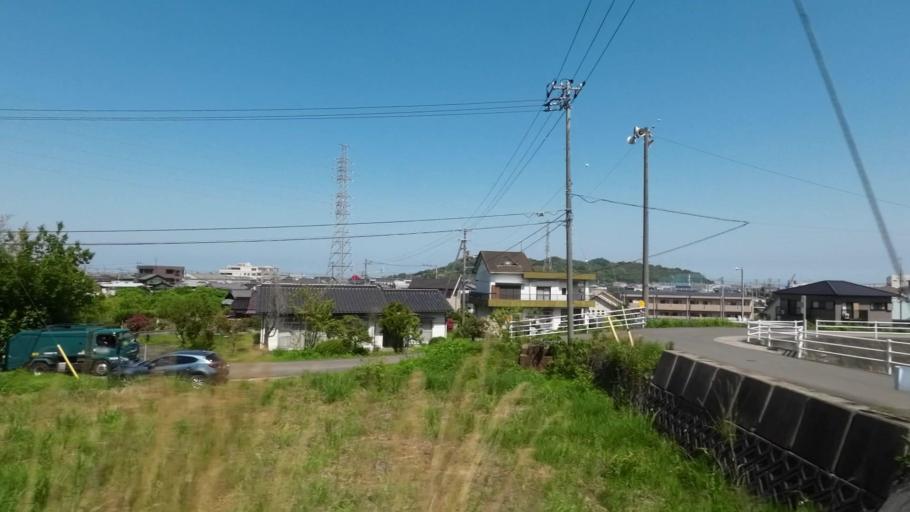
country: JP
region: Ehime
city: Niihama
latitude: 33.9720
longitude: 133.3340
